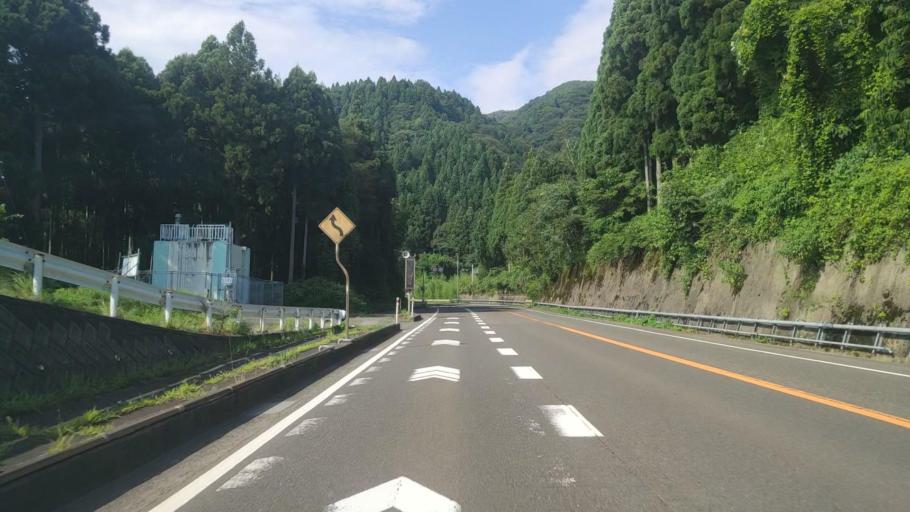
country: JP
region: Fukui
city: Tsuruga
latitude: 35.7553
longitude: 136.1057
